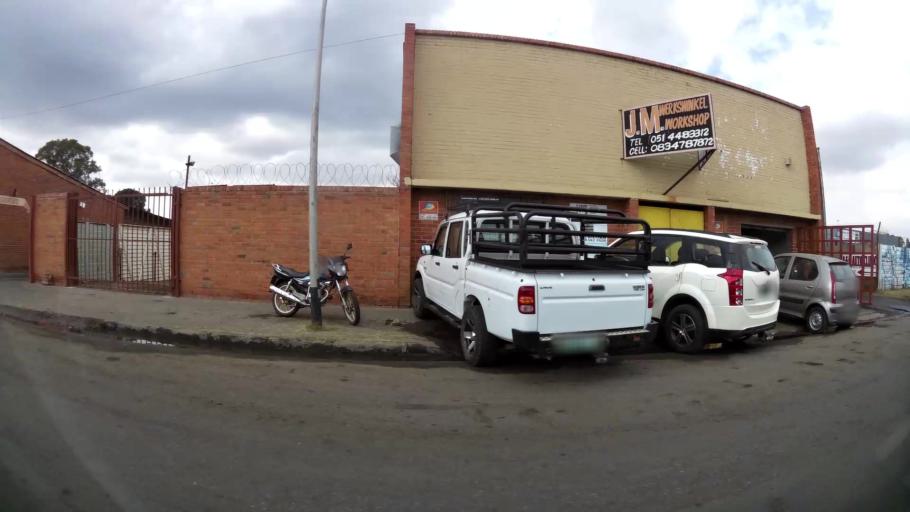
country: ZA
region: Orange Free State
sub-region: Mangaung Metropolitan Municipality
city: Bloemfontein
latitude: -29.1272
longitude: 26.2262
